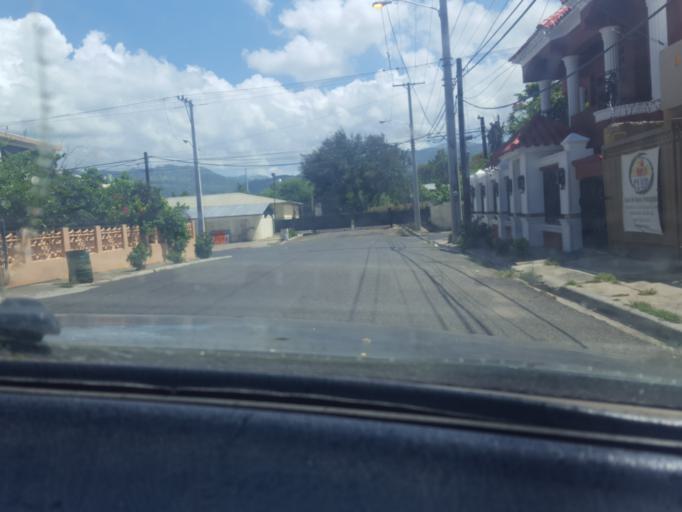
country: DO
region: Santiago
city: Santiago de los Caballeros
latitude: 19.4949
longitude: -70.6965
